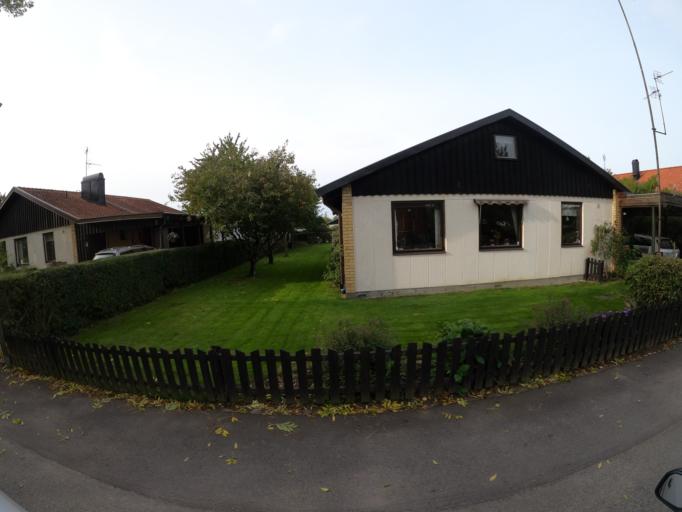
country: SE
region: Skane
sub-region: Lunds Kommun
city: Lund
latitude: 55.7492
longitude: 13.1977
